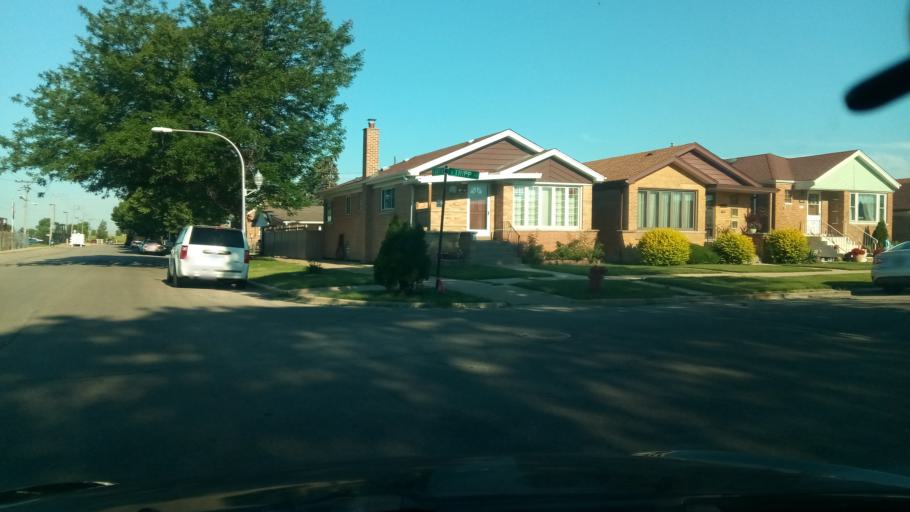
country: US
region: Illinois
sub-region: Cook County
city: Hometown
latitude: 41.7677
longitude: -87.7284
